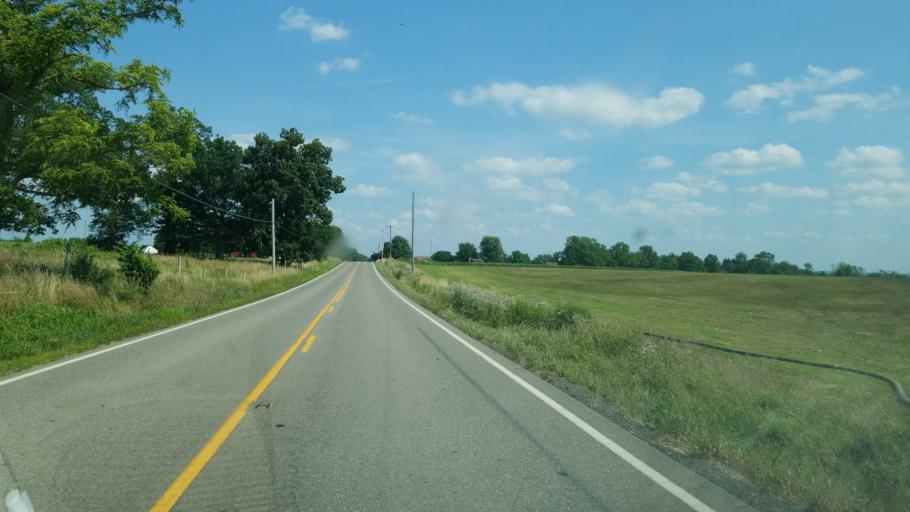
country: US
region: Ohio
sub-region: Huron County
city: Greenwich
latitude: 40.9368
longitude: -82.5450
